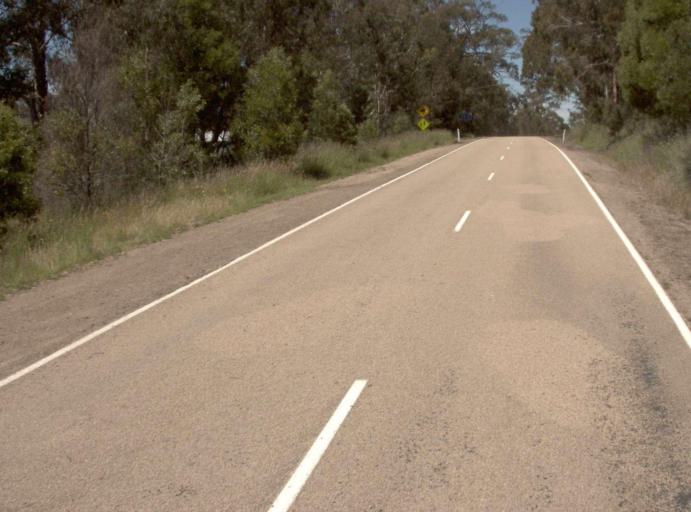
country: AU
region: Victoria
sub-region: East Gippsland
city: Lakes Entrance
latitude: -37.2179
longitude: 148.2666
